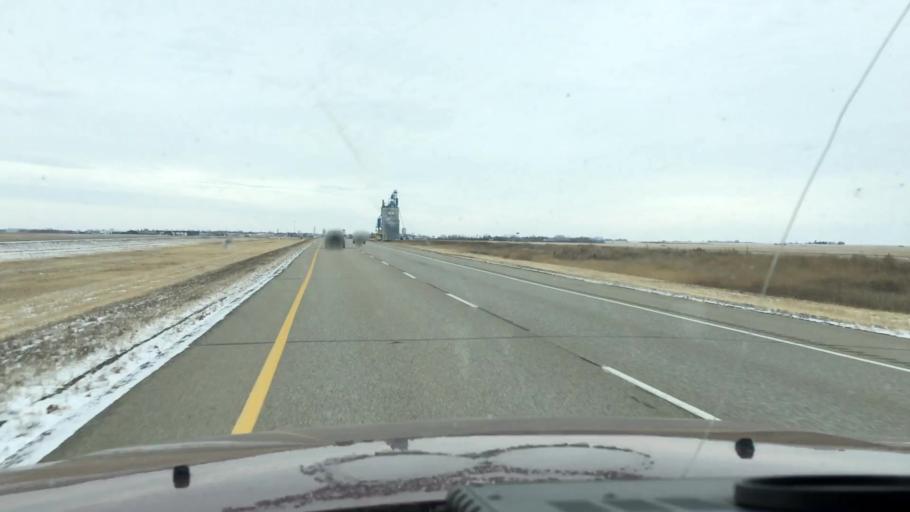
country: CA
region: Saskatchewan
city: Watrous
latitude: 51.2876
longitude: -106.0254
